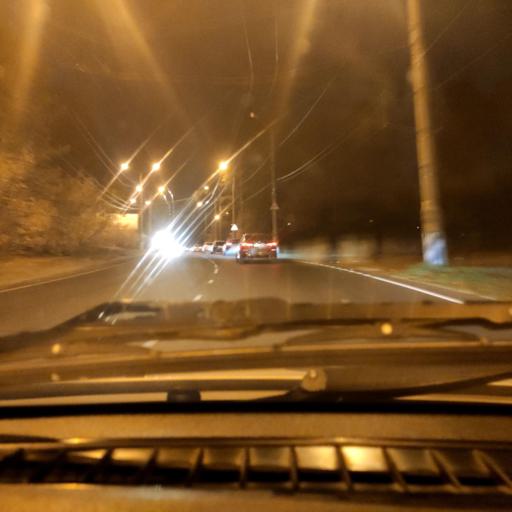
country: RU
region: Samara
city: Tol'yatti
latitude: 53.4776
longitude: 49.3497
